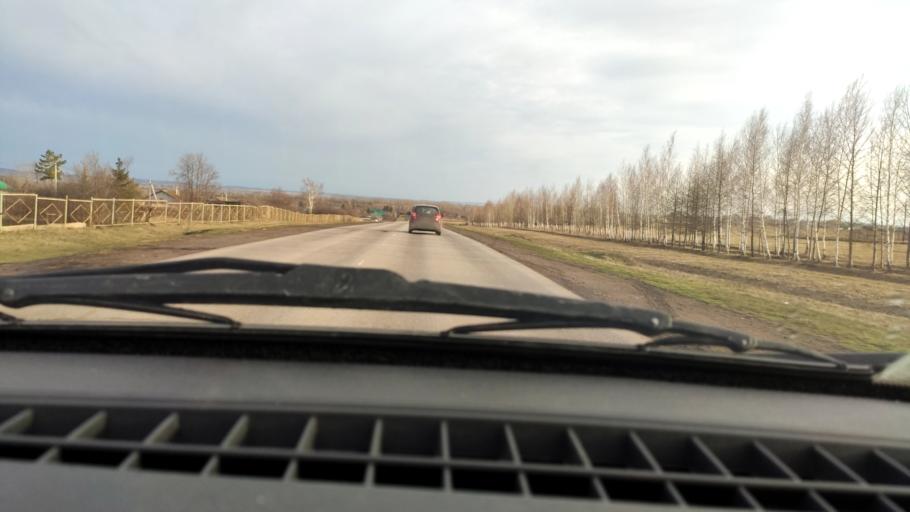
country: RU
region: Bashkortostan
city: Davlekanovo
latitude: 54.3763
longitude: 55.1952
